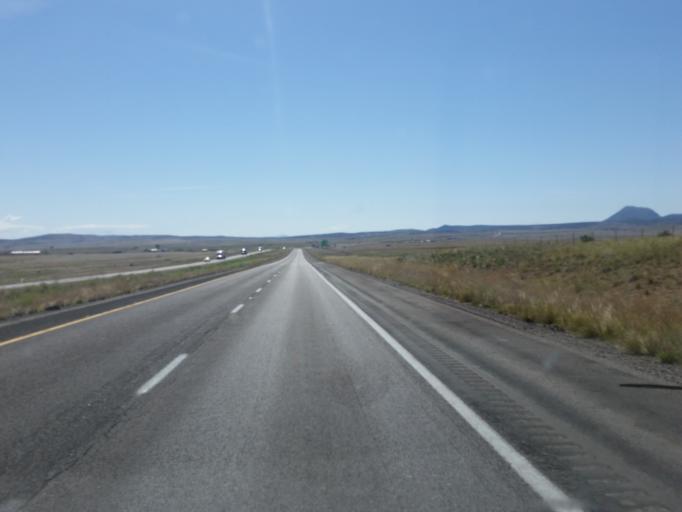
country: US
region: Arizona
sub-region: Mohave County
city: Peach Springs
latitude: 35.3177
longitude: -112.8810
